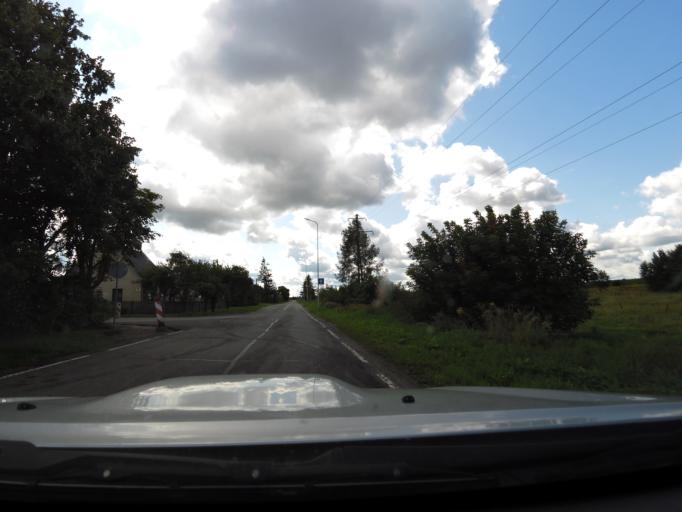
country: LV
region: Daugavpils
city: Daugavpils
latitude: 55.8710
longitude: 26.4920
